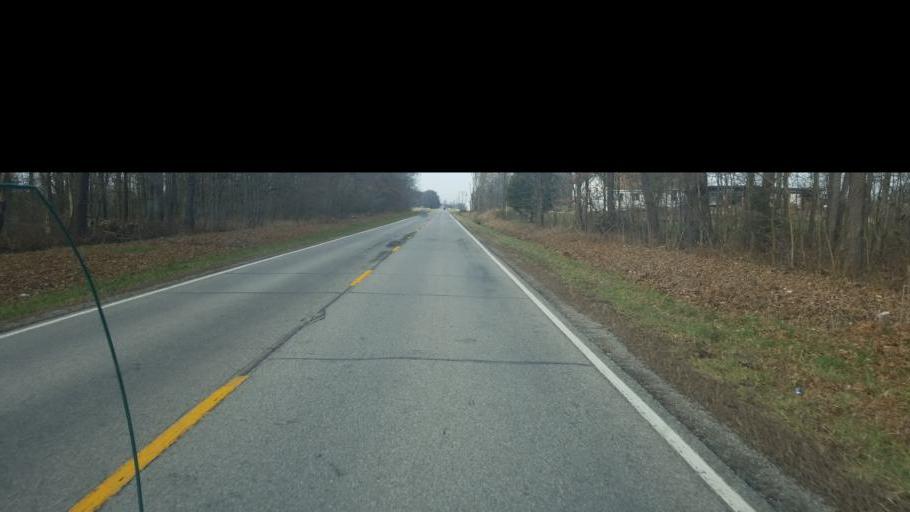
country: US
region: Illinois
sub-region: Hamilton County
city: McLeansboro
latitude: 37.9769
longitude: -88.4831
